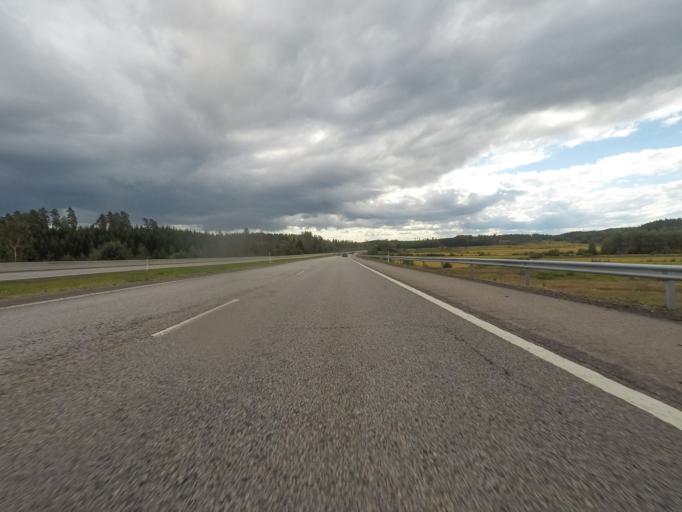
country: FI
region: Paijanne Tavastia
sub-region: Lahti
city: Nastola
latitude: 61.0820
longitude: 25.8924
